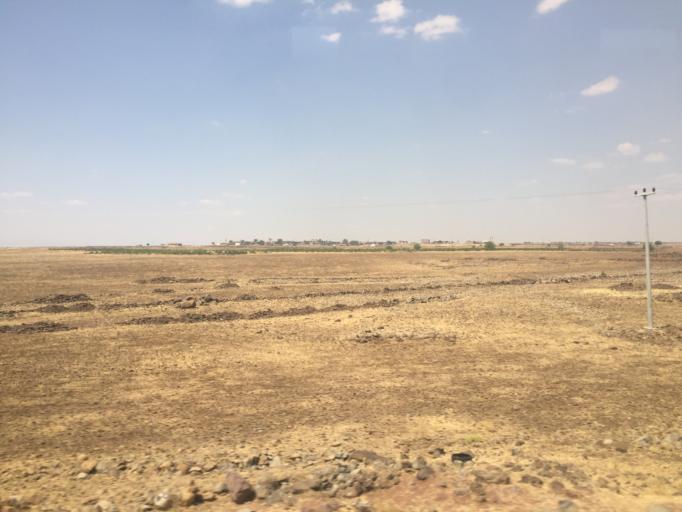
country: TR
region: Sanliurfa
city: Siverek
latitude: 37.7739
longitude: 39.4501
